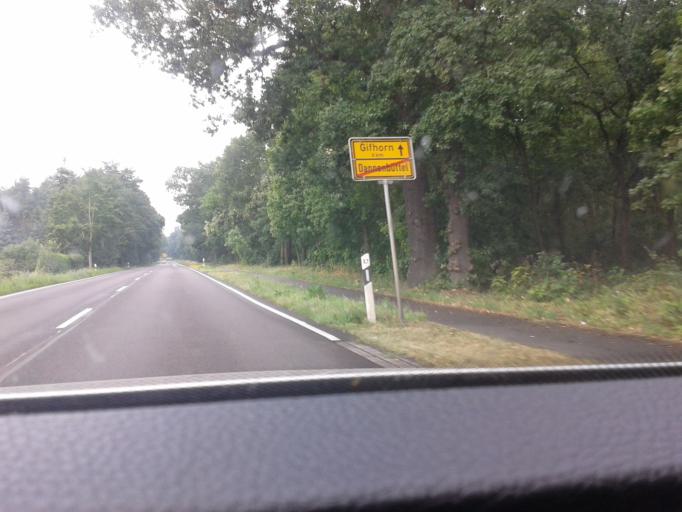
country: DE
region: Lower Saxony
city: Sassenburg
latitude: 52.4957
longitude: 10.6191
